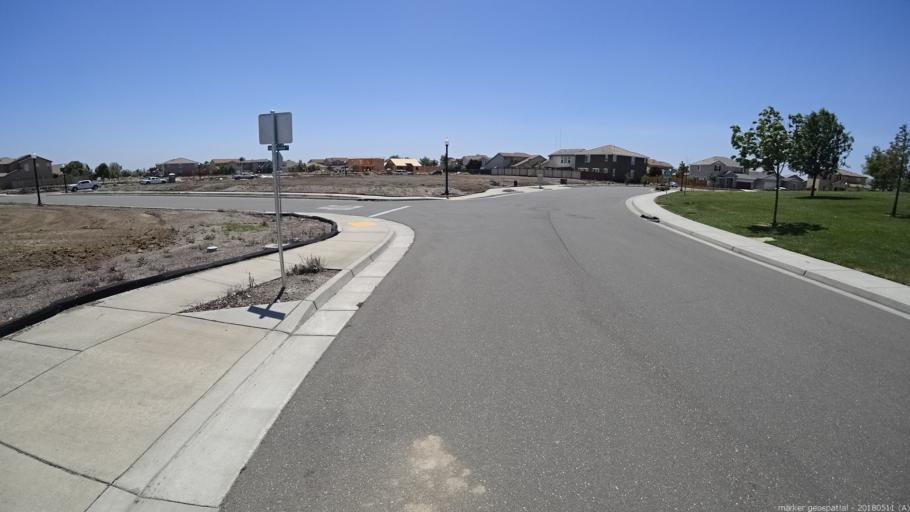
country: US
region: California
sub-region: Yolo County
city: West Sacramento
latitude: 38.6466
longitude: -121.5484
